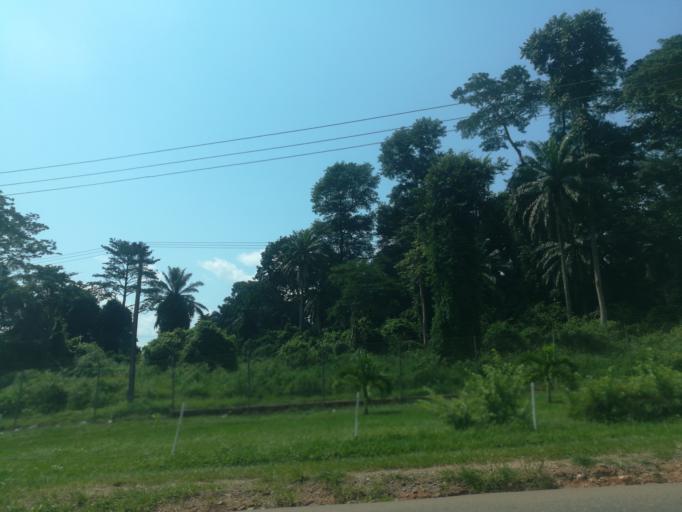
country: NG
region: Oyo
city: Moniya
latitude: 7.4909
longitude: 3.9137
